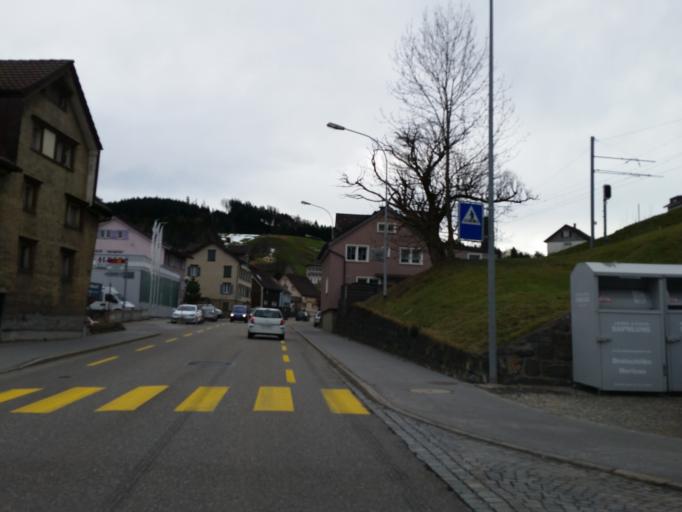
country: CH
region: Appenzell Ausserrhoden
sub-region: Bezirk Hinterland
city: Herisau
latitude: 47.3754
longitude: 9.2800
